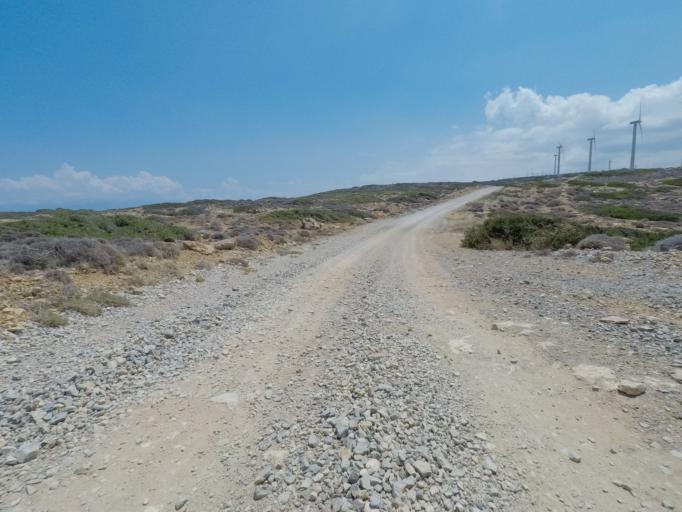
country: GR
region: Crete
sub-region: Nomos Lasithiou
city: Elounda
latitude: 35.3302
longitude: 25.7595
